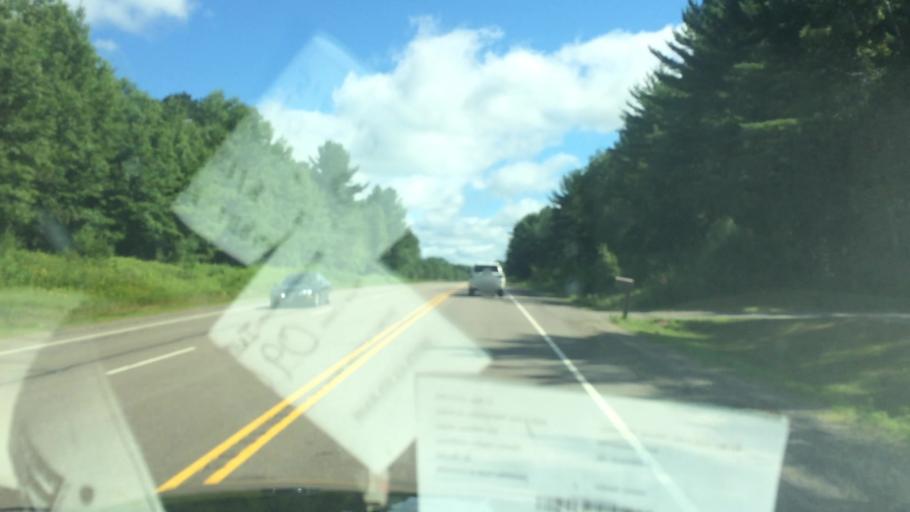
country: US
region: Wisconsin
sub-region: Oneida County
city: Rhinelander
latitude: 45.5978
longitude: -89.5629
